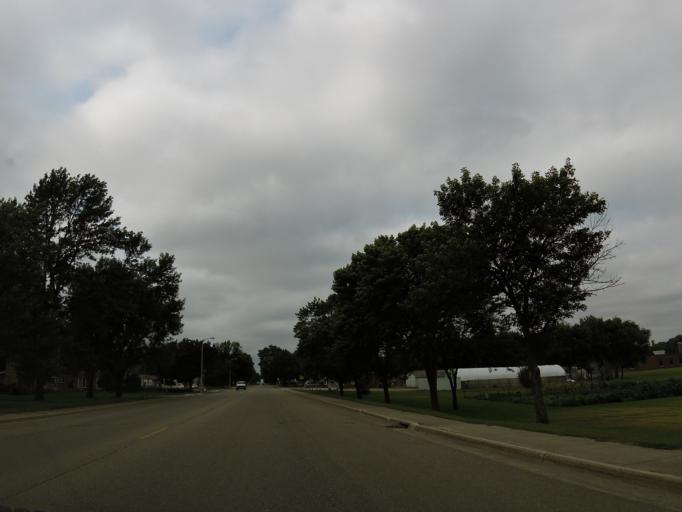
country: US
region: Minnesota
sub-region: Renville County
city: Renville
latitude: 44.7893
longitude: -95.2055
